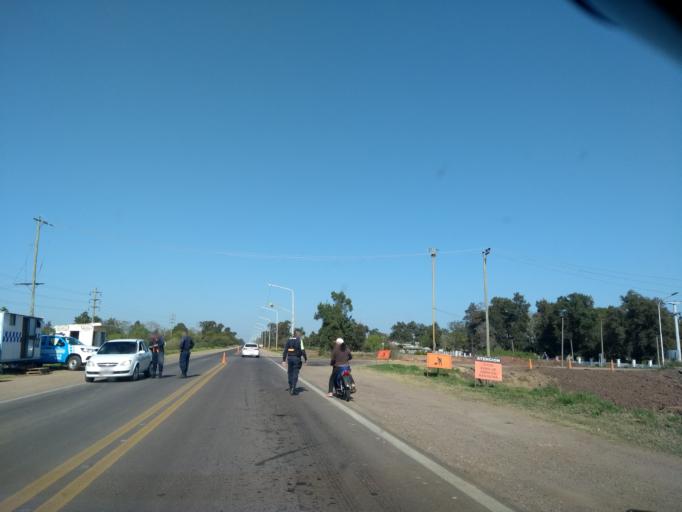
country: AR
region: Chaco
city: Presidencia Roque Saenz Pena
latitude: -26.7777
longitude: -60.4031
